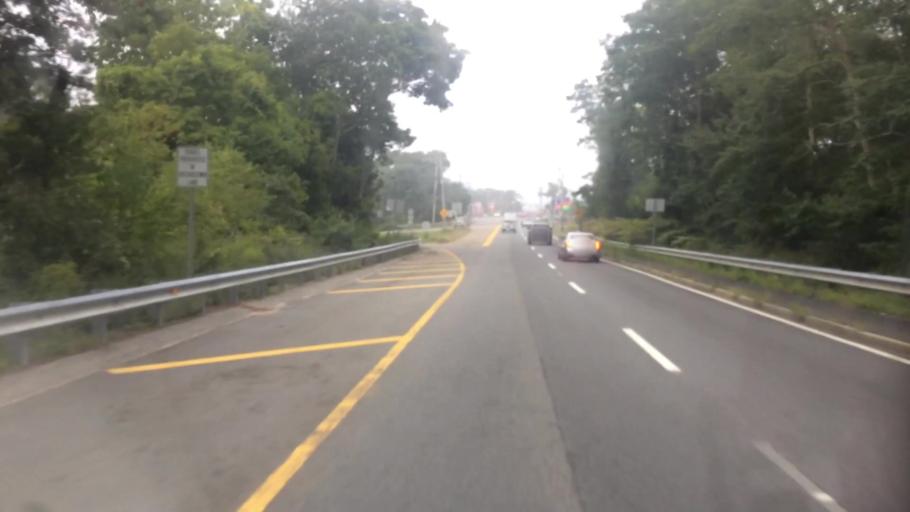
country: US
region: Massachusetts
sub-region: Plymouth County
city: Onset
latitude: 41.7600
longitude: -70.6701
